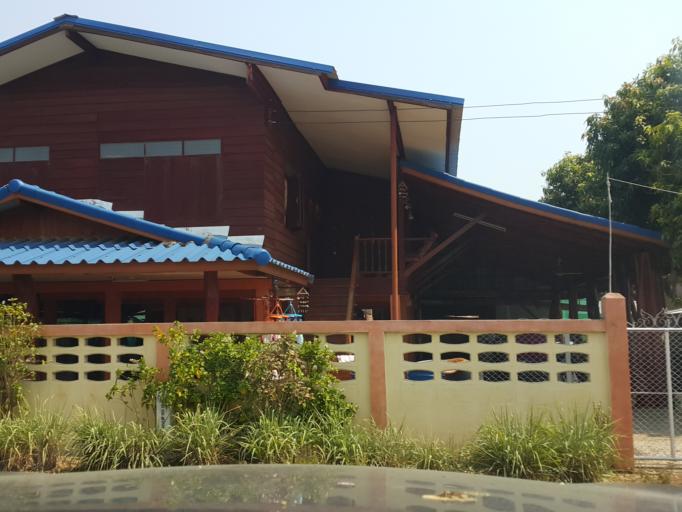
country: TH
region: Sukhothai
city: Thung Saliam
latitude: 17.3124
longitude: 99.5572
